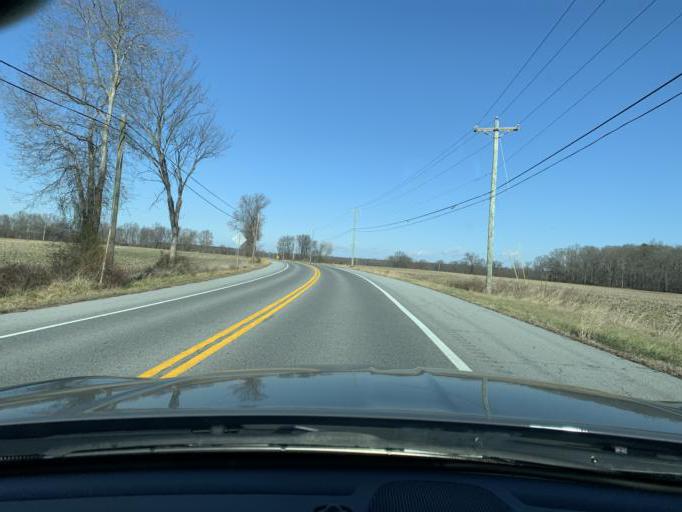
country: US
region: Maryland
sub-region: Queen Anne's County
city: Centreville
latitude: 39.0801
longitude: -76.0334
